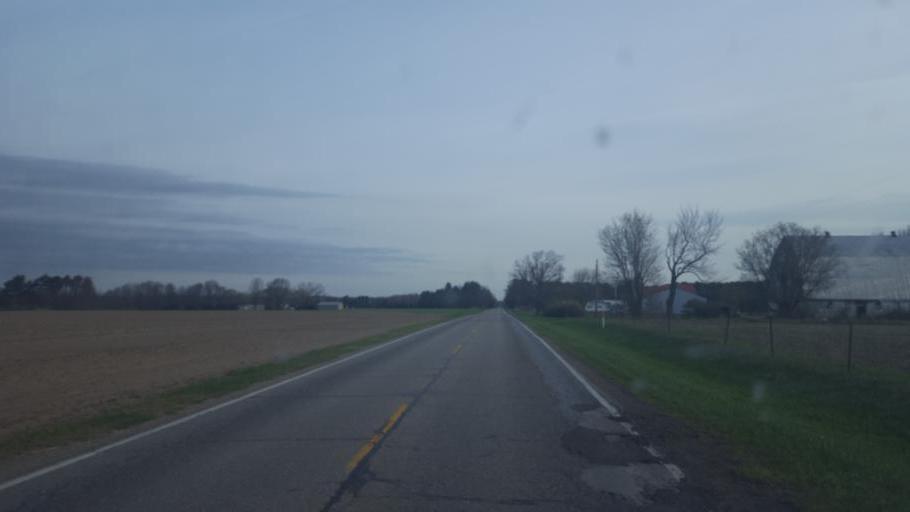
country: US
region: Michigan
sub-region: Isabella County
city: Lake Isabella
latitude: 43.5353
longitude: -84.9864
